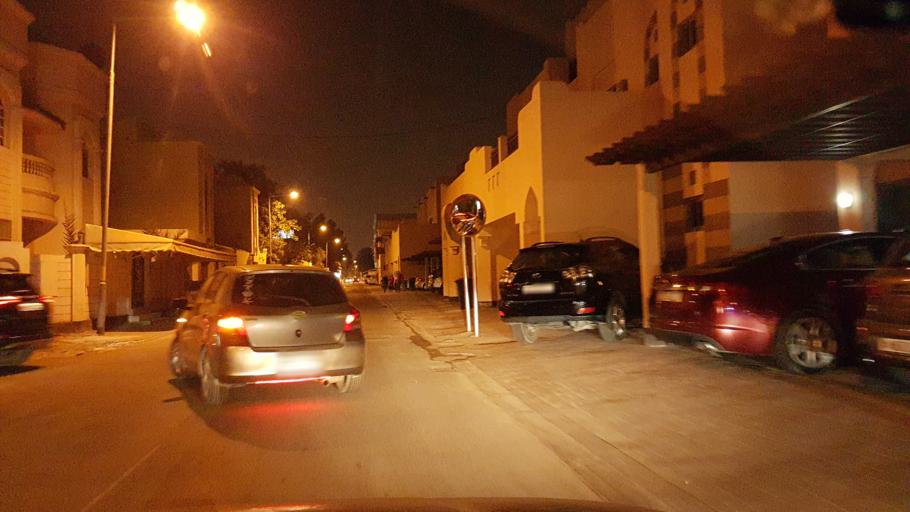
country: BH
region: Manama
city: Manama
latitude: 26.2197
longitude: 50.5849
